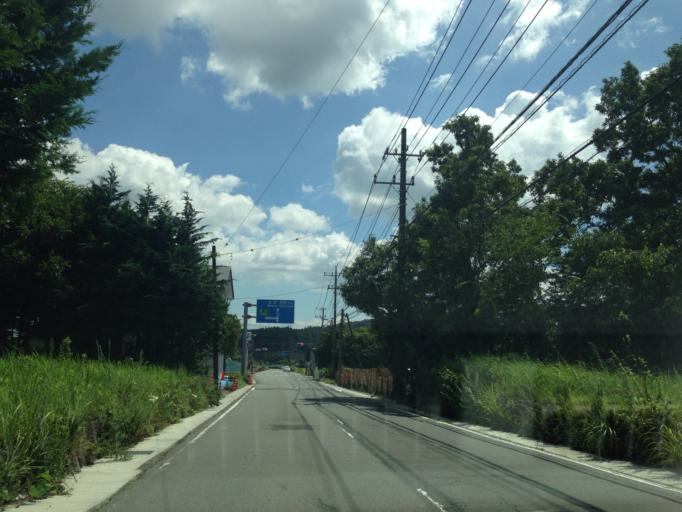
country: JP
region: Shizuoka
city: Gotemba
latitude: 35.2314
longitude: 138.8778
